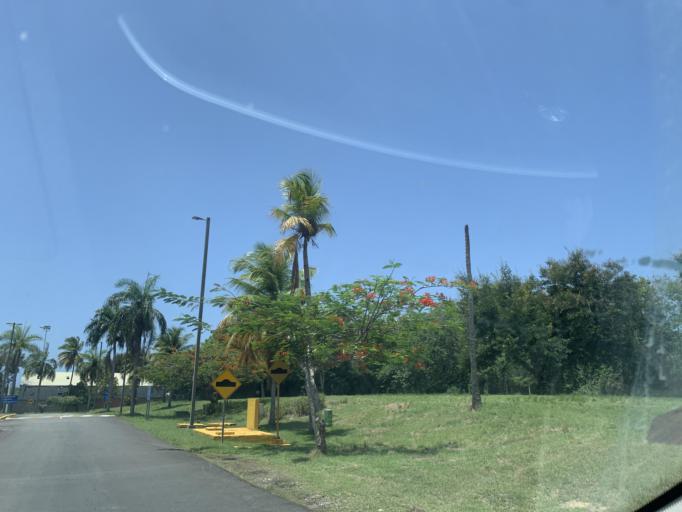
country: DO
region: Puerto Plata
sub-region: Puerto Plata
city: Puerto Plata
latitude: 19.7546
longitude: -70.5617
